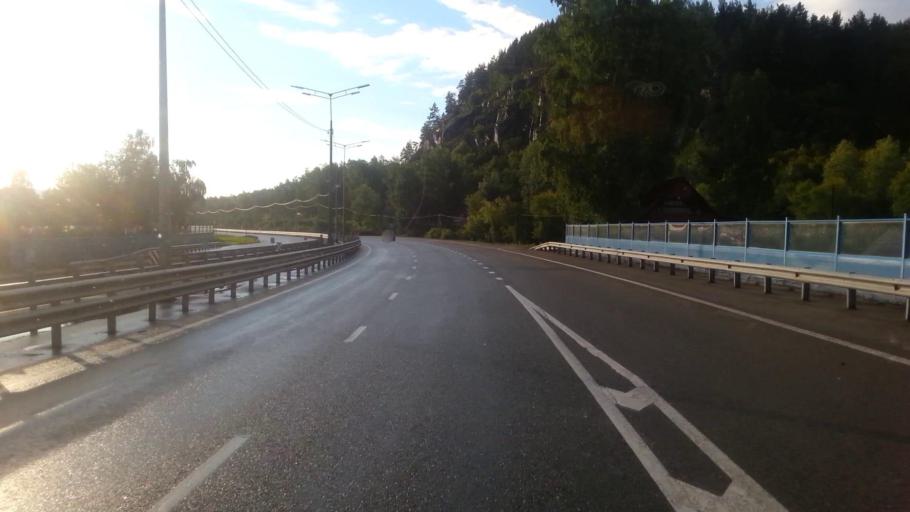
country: RU
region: Altay
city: Souzga
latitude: 51.9184
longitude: 85.8588
